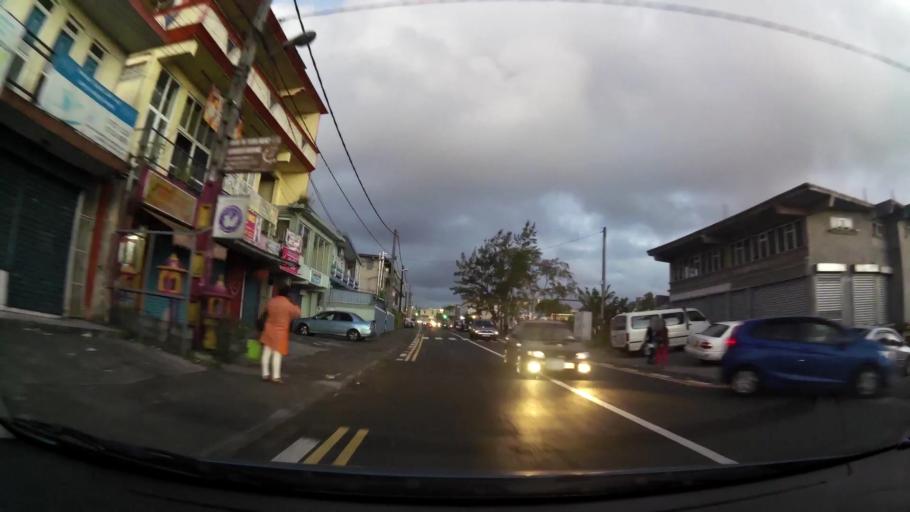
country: MU
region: Plaines Wilhems
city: Curepipe
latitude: -20.3017
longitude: 57.5214
